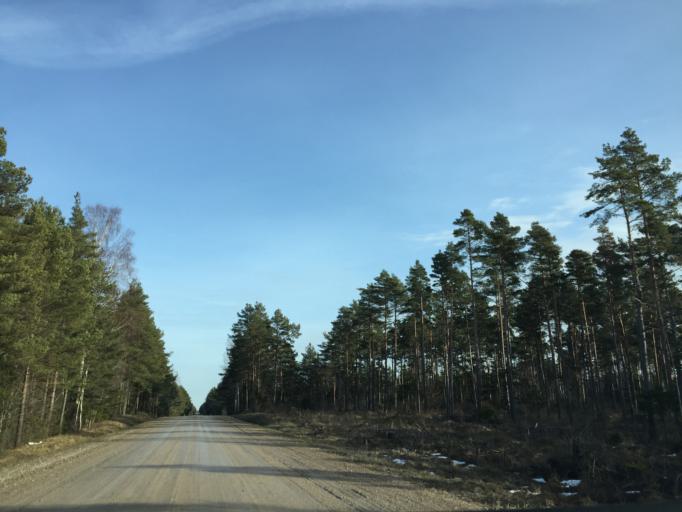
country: EE
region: Saare
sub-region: Kuressaare linn
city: Kuressaare
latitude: 58.3046
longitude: 21.9657
